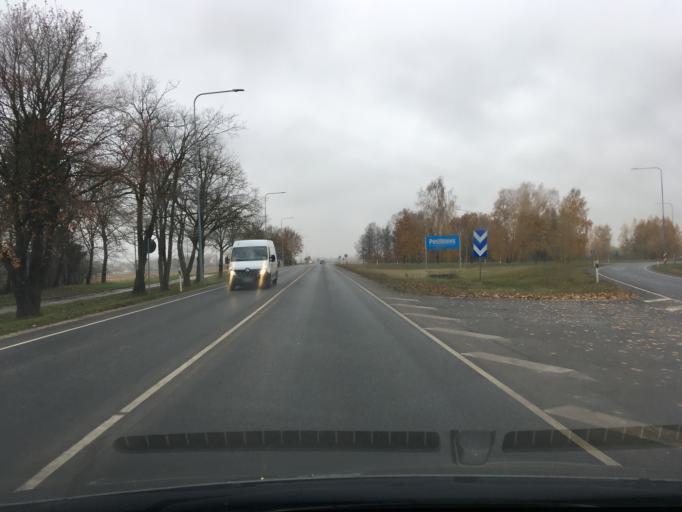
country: EE
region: Tartu
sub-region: Tartu linn
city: Tartu
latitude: 58.4082
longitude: 26.7083
